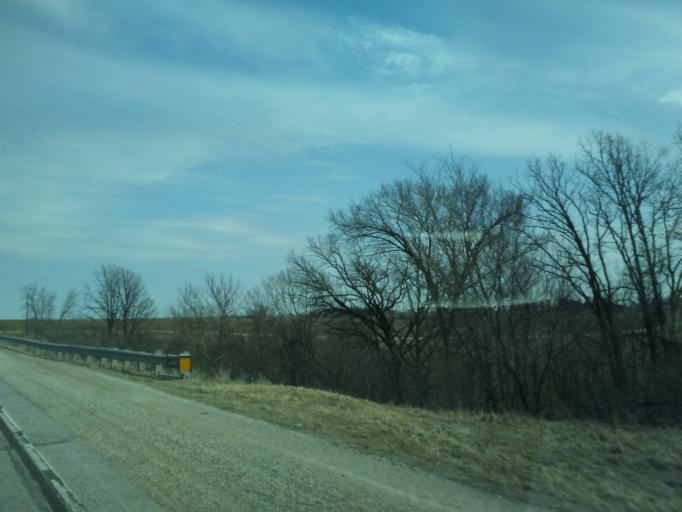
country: US
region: Iowa
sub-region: Allamakee County
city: Waukon
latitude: 43.2406
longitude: -91.5489
